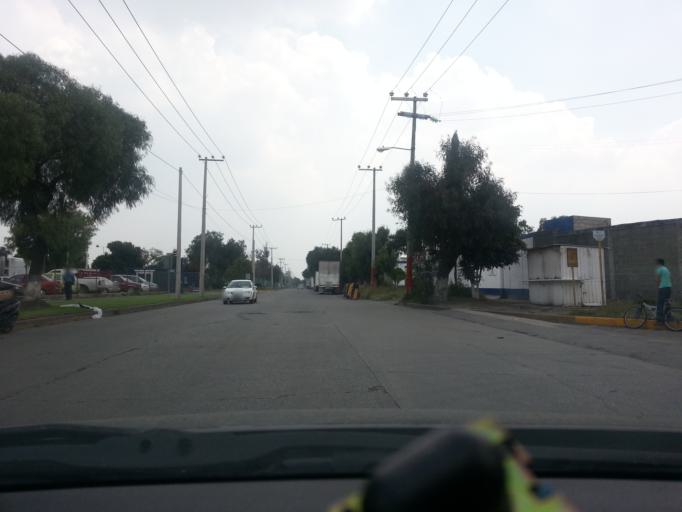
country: MX
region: Mexico
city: Cuautitlan Izcalli
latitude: 19.6637
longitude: -99.2043
